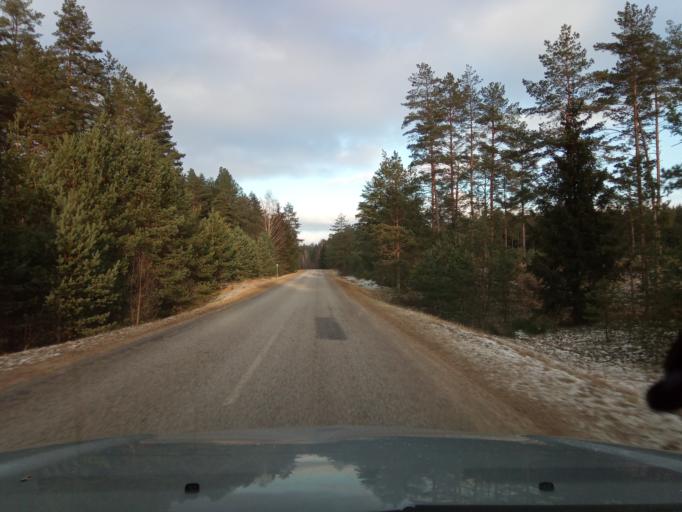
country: LT
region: Alytaus apskritis
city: Varena
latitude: 54.1000
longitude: 24.4274
